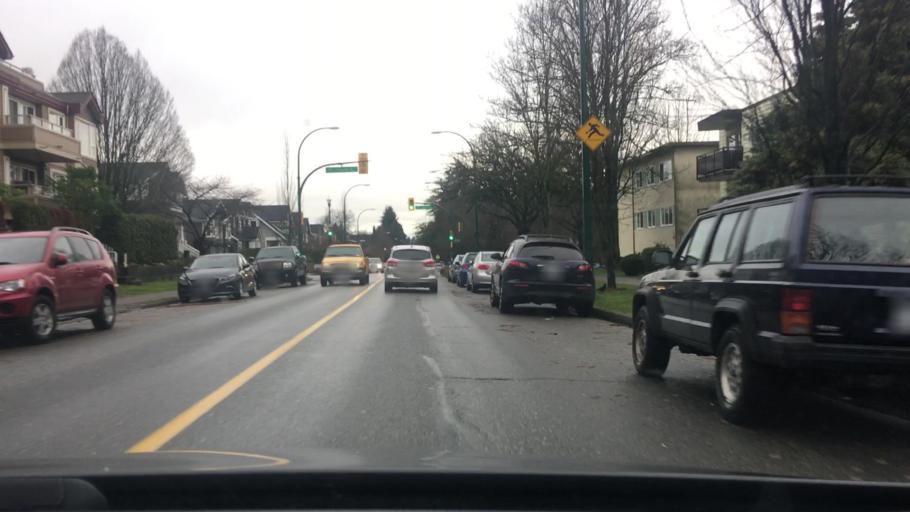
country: CA
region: British Columbia
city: Vancouver
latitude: 49.2567
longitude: -123.1040
